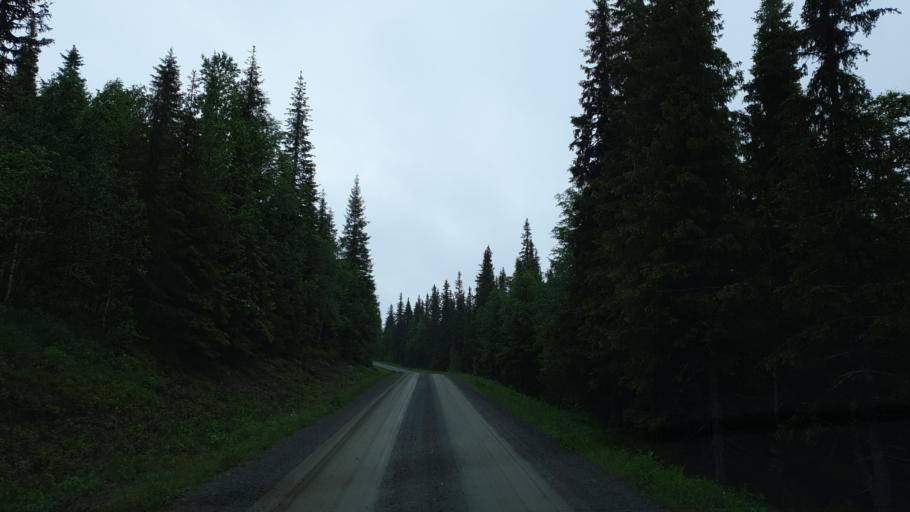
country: SE
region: Vaesterbotten
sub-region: Vilhelmina Kommun
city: Sjoberg
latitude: 65.3314
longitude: 15.9073
